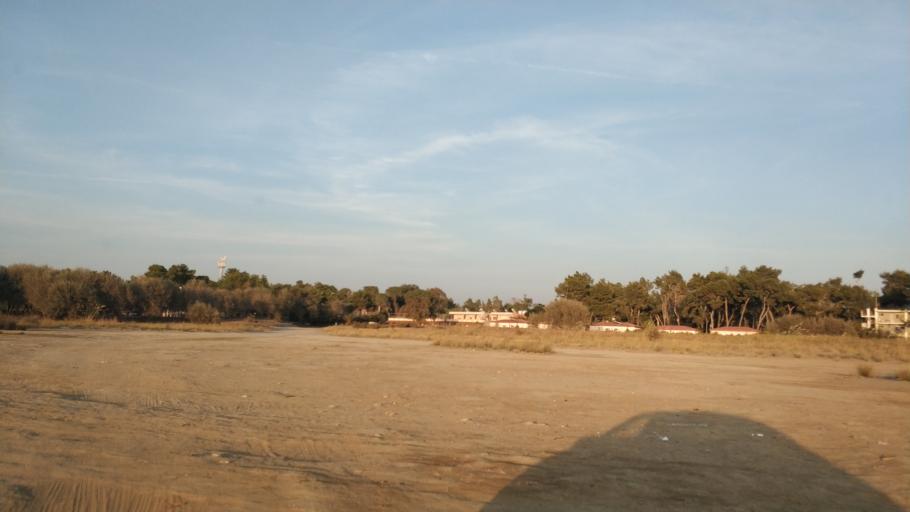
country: AL
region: Fier
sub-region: Rrethi i Lushnjes
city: Divjake
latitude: 40.9712
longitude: 19.4770
